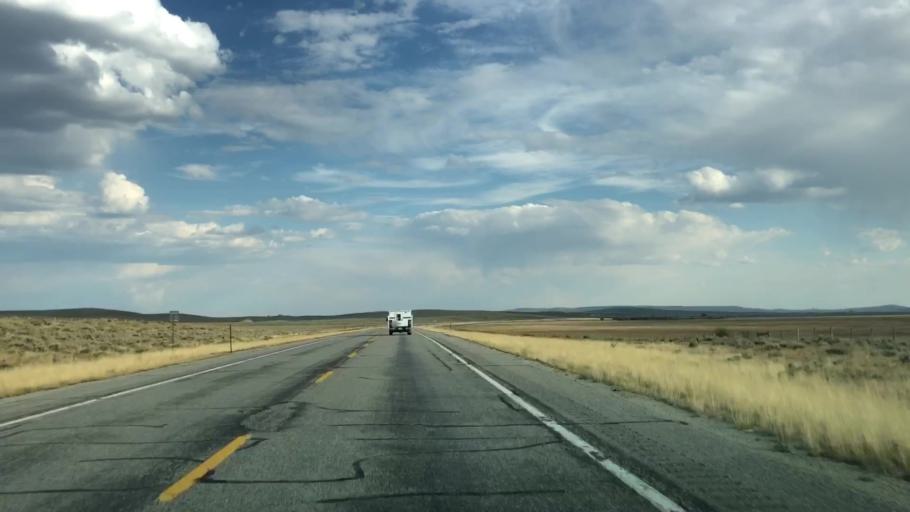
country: US
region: Wyoming
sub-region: Sublette County
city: Pinedale
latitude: 43.0371
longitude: -110.1348
